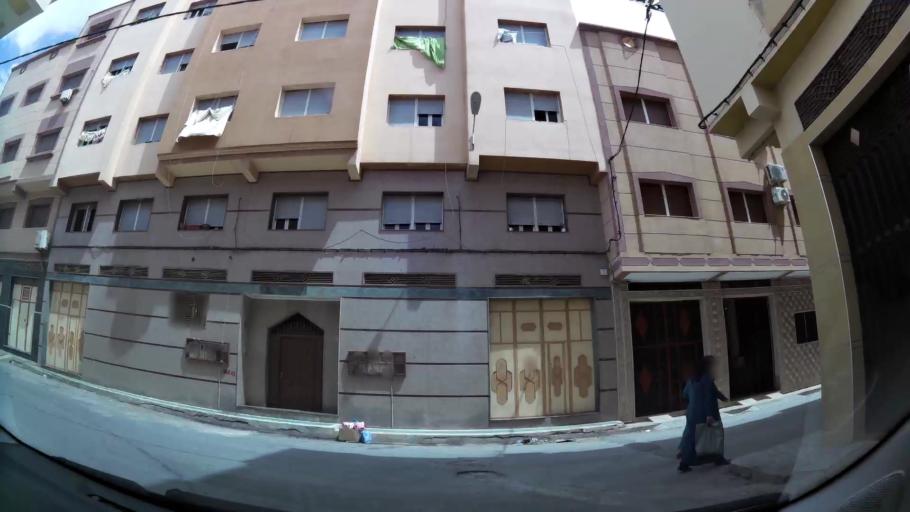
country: MA
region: Oriental
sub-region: Nador
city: Nador
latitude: 35.1655
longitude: -2.9278
